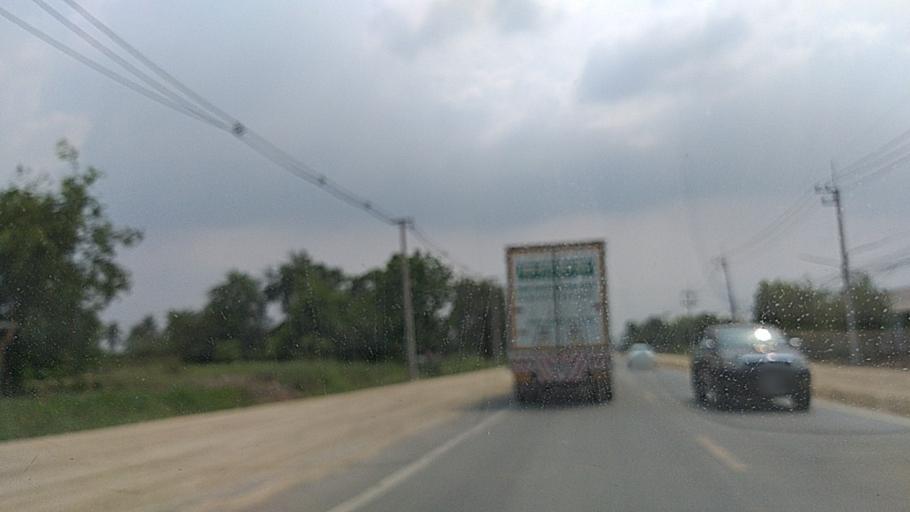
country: TH
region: Chon Buri
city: Ban Bueng
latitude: 13.3479
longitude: 101.1948
